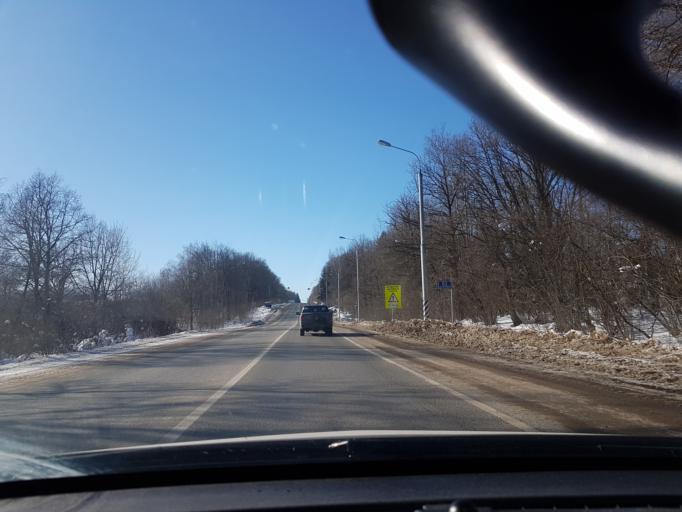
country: RU
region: Moskovskaya
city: Kostrovo
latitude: 55.9114
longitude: 36.7646
